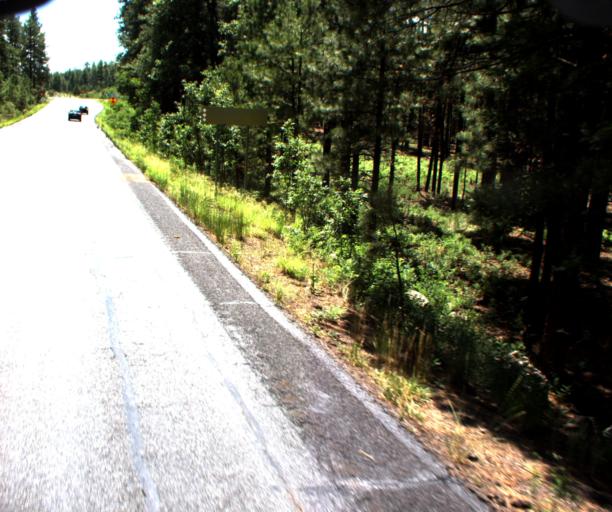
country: US
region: Arizona
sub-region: Gila County
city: Pine
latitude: 34.4566
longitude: -111.4382
